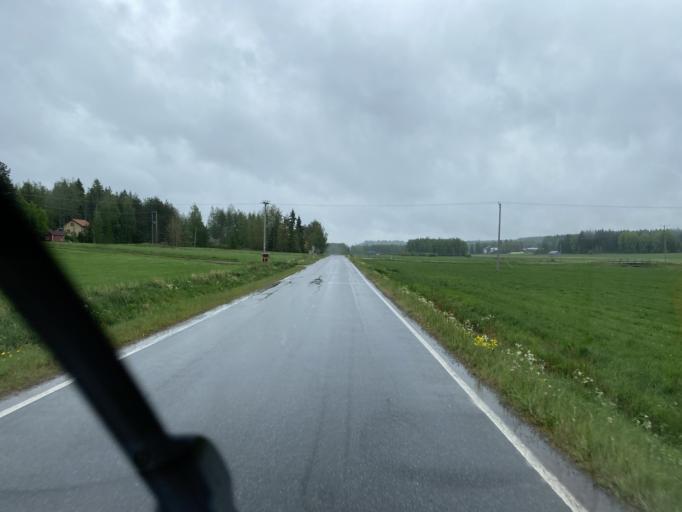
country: FI
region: Haeme
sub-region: Forssa
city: Humppila
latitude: 61.0428
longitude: 23.3921
